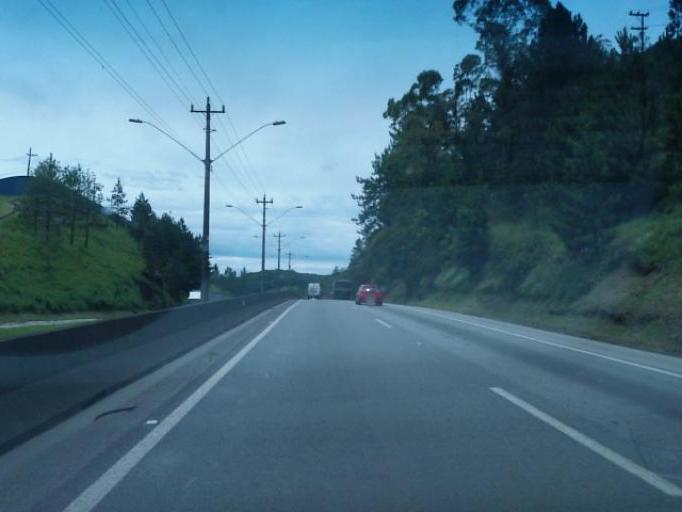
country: BR
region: Sao Paulo
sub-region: Sao Lourenco Da Serra
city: Sao Lourenco da Serra
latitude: -23.8996
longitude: -46.9885
